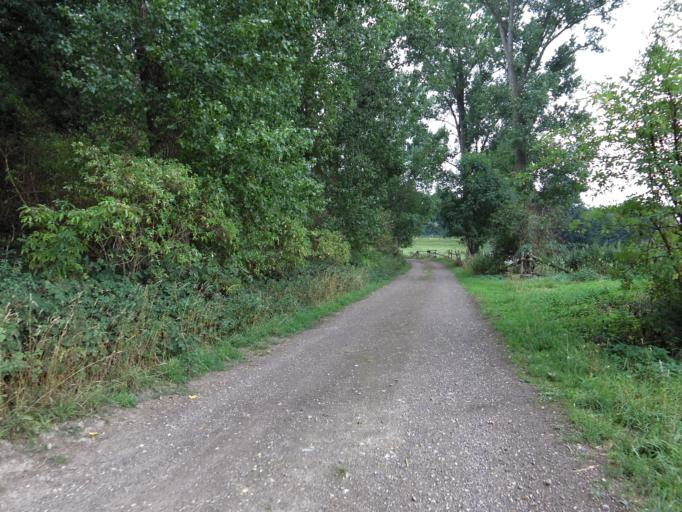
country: DE
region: North Rhine-Westphalia
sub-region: Regierungsbezirk Koln
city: Linnich
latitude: 50.9643
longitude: 6.2597
